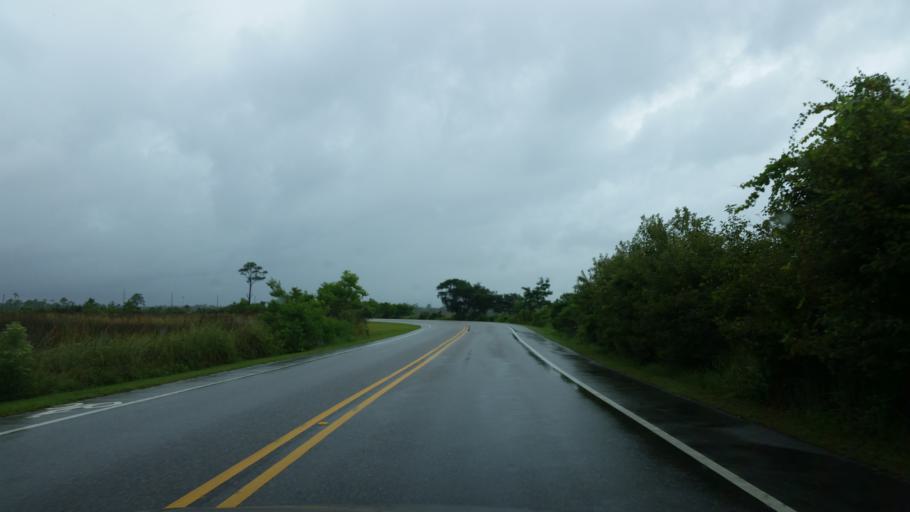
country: US
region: Alabama
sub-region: Baldwin County
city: Gulf Shores
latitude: 30.2552
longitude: -87.6706
